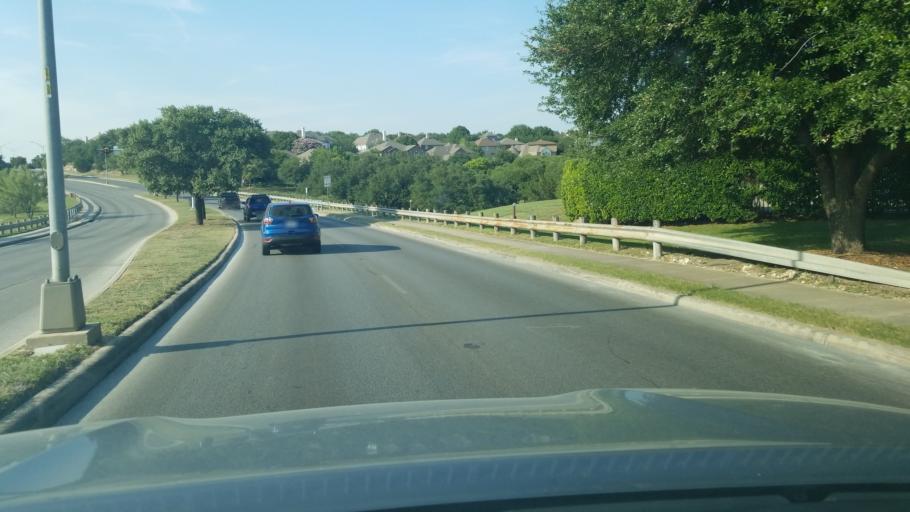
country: US
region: Texas
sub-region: Bexar County
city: Hollywood Park
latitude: 29.6382
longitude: -98.5067
